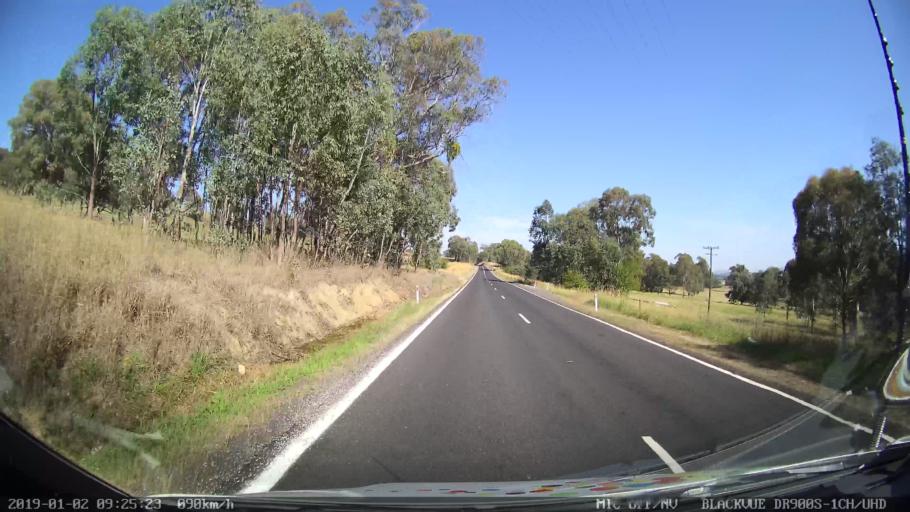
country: AU
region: New South Wales
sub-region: Tumut Shire
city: Tumut
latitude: -35.3667
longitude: 148.2869
